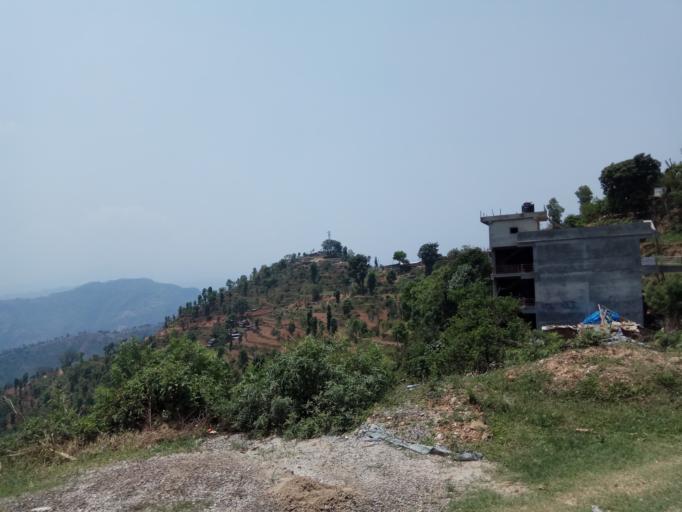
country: NP
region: Central Region
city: Kirtipur
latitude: 27.8965
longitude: 85.0673
